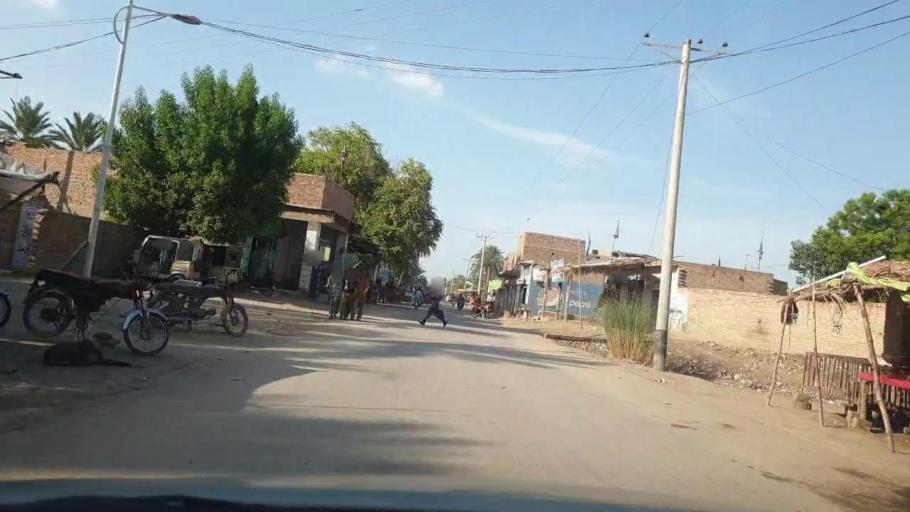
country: PK
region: Sindh
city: Sukkur
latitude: 27.6566
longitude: 68.8408
